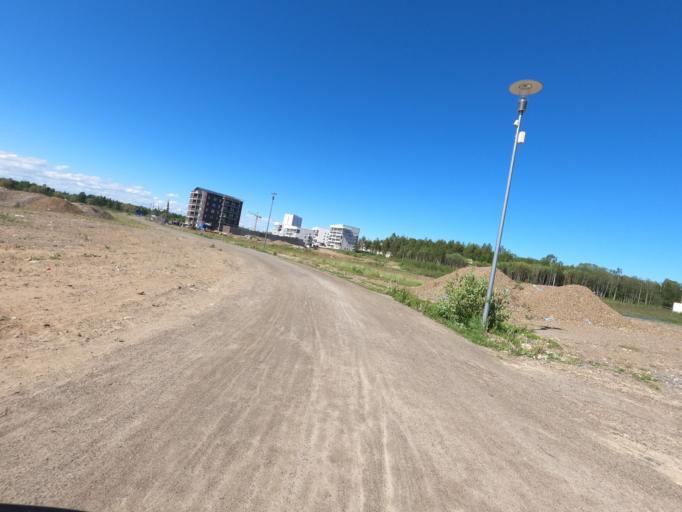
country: FI
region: North Karelia
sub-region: Joensuu
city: Joensuu
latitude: 62.5878
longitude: 29.7615
